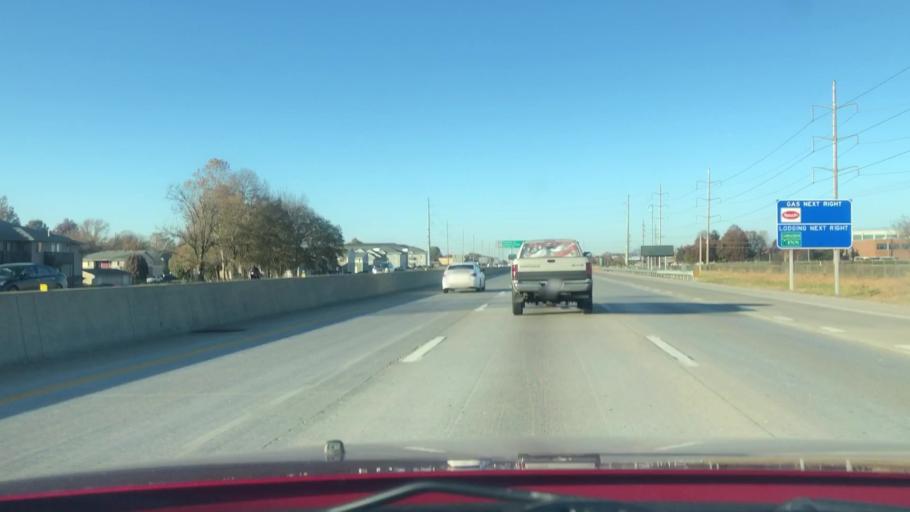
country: US
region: Missouri
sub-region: Greene County
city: Springfield
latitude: 37.1663
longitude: -93.2243
